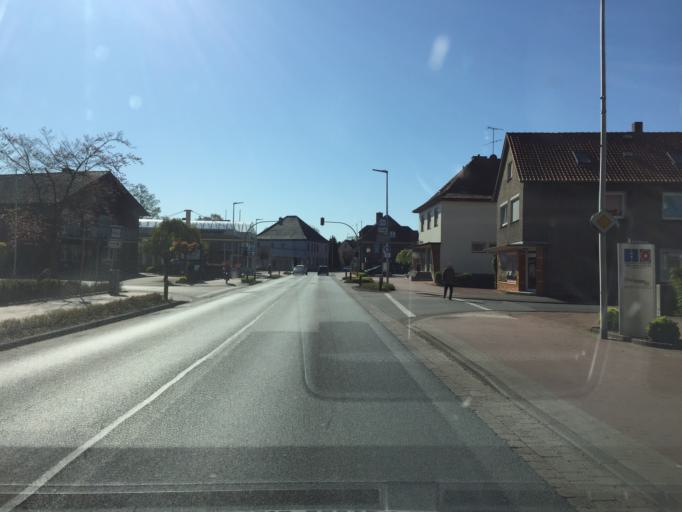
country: DE
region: Lower Saxony
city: Wagenfeld
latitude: 52.5485
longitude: 8.5888
